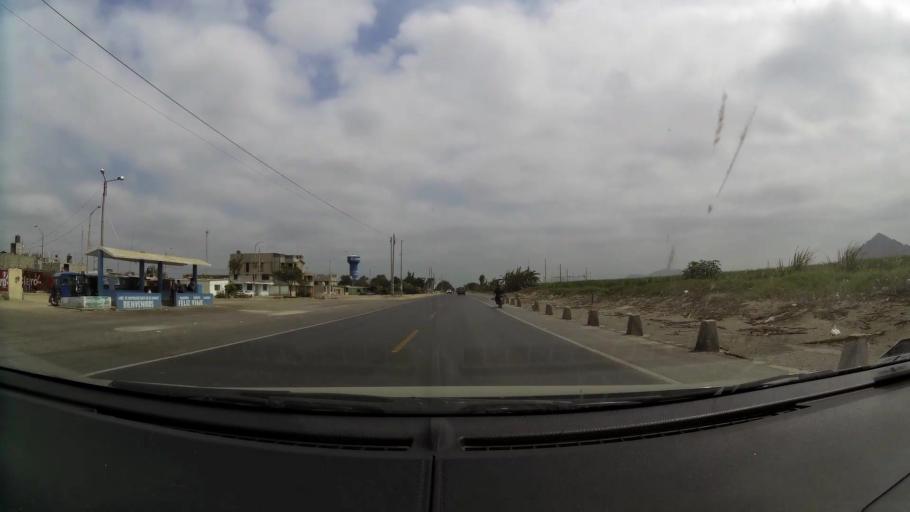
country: PE
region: La Libertad
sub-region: Ascope
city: Chocope
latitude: -7.8043
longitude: -79.1943
